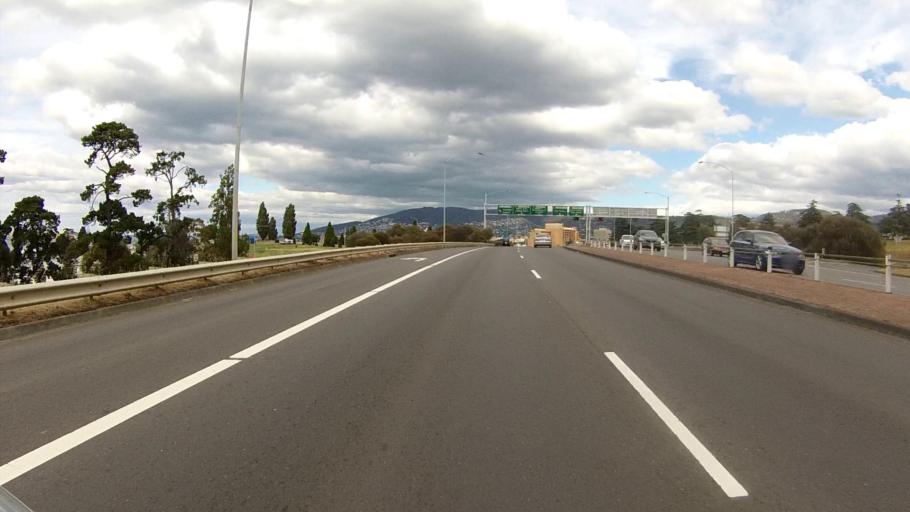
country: AU
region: Tasmania
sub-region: Hobart
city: Hobart
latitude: -42.8742
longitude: 147.3343
